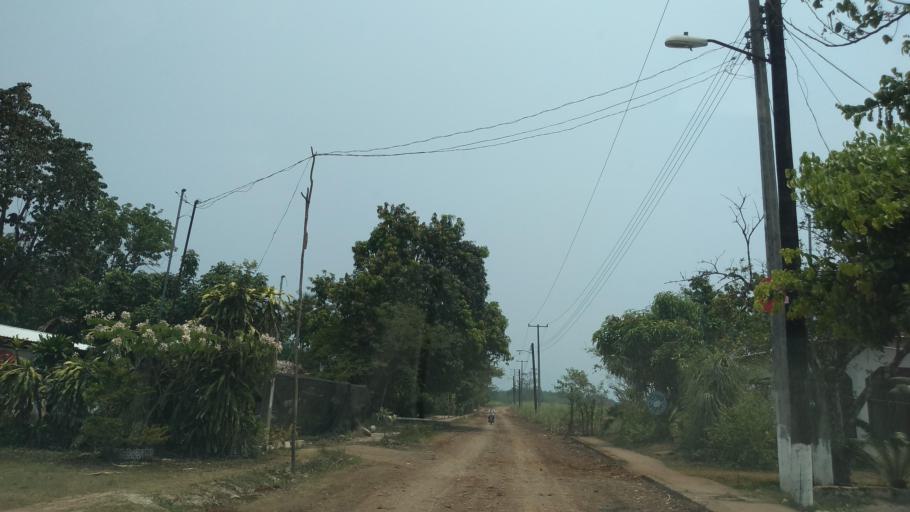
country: MX
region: Puebla
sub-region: San Sebastian Tlacotepec
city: San Martin Mazateopan
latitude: 18.4951
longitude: -96.7797
